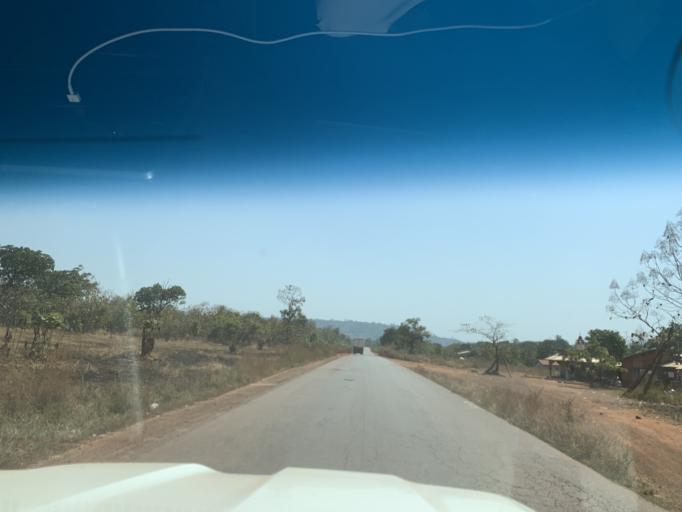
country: GN
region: Kindia
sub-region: Kindia
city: Kindia
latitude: 9.9953
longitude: -12.7528
